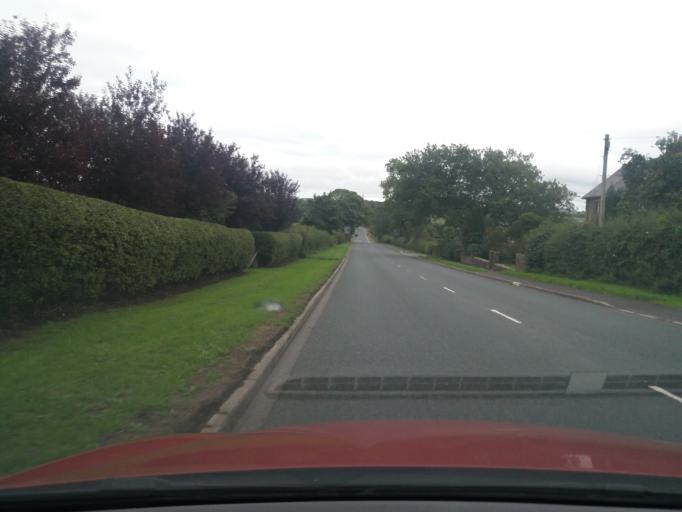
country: GB
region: England
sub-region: Lancashire
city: Chorley
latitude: 53.7238
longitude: -2.5749
